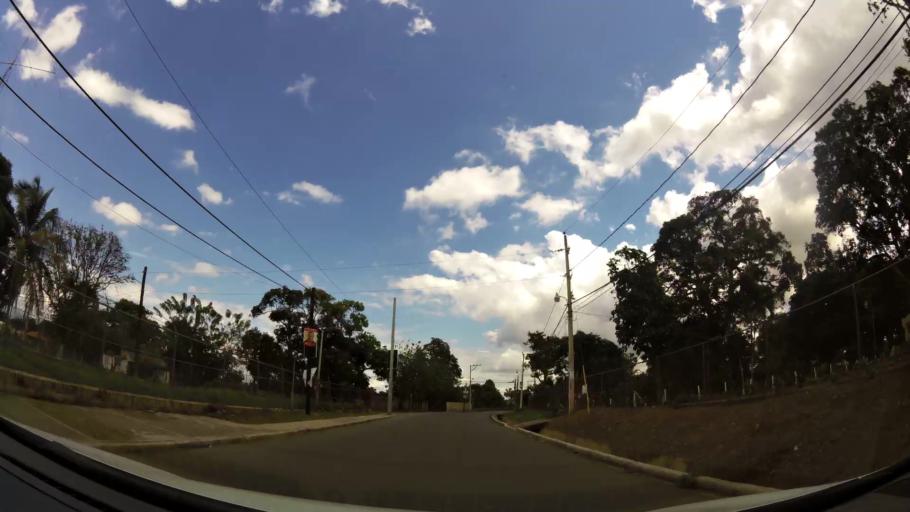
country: DO
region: Santiago
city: Licey al Medio
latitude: 19.3922
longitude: -70.6415
